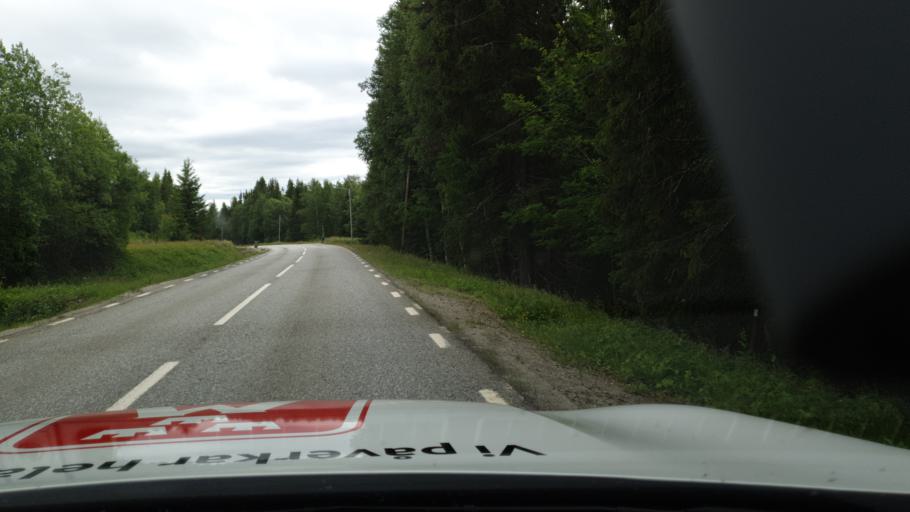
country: SE
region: Vaesterbotten
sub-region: Lycksele Kommun
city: Soderfors
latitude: 64.6500
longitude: 17.8498
